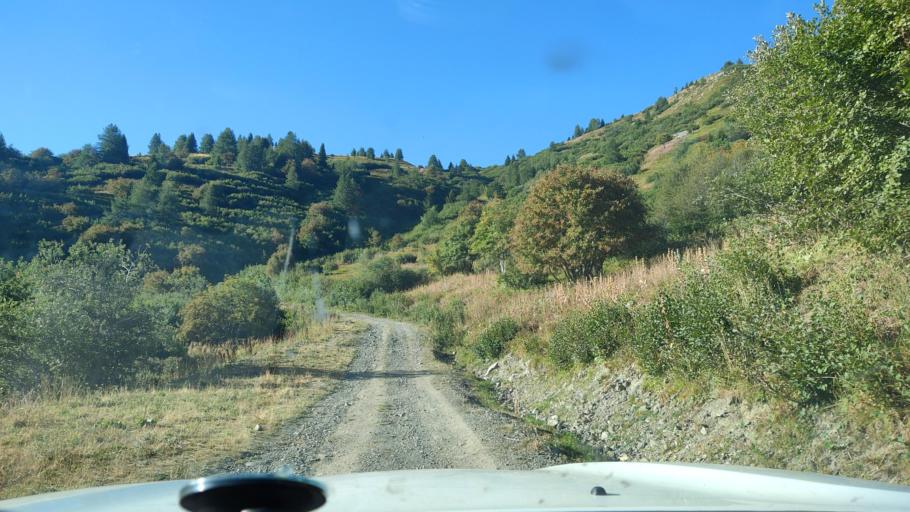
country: FR
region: Rhone-Alpes
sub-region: Departement de la Savoie
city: Valloire
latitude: 45.1748
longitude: 6.4665
